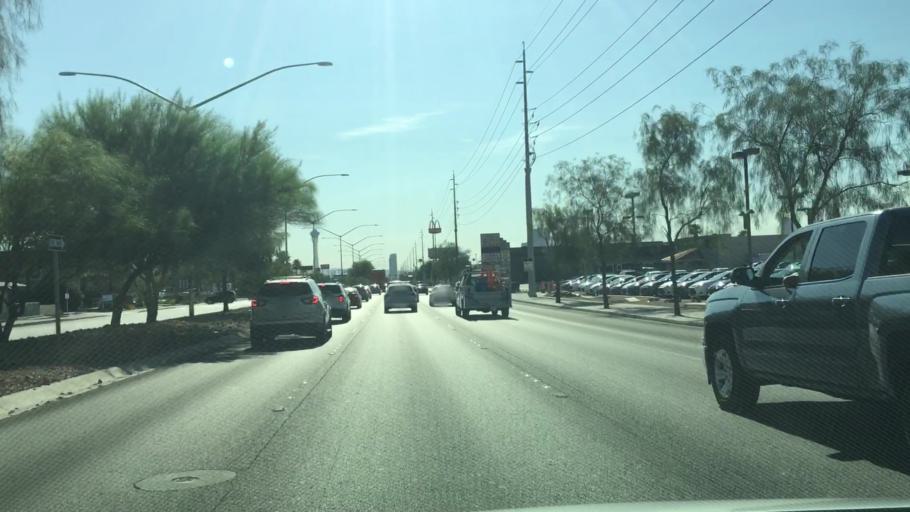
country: US
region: Nevada
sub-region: Clark County
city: Spring Valley
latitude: 36.1444
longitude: -115.2054
